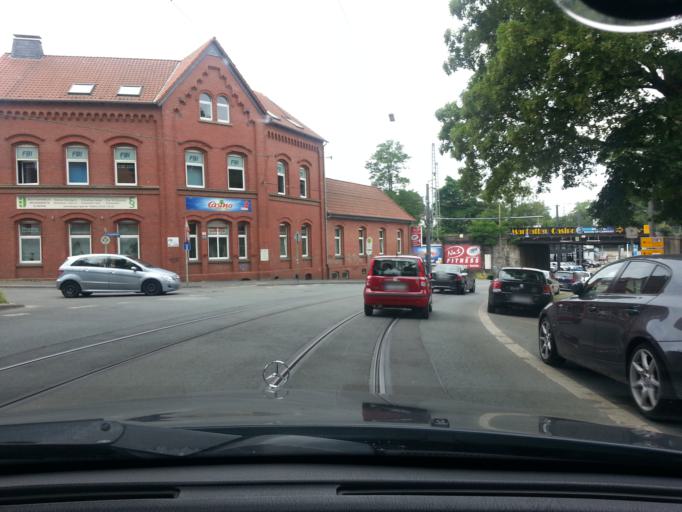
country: DE
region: North Rhine-Westphalia
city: Witten
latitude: 51.4488
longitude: 7.3272
